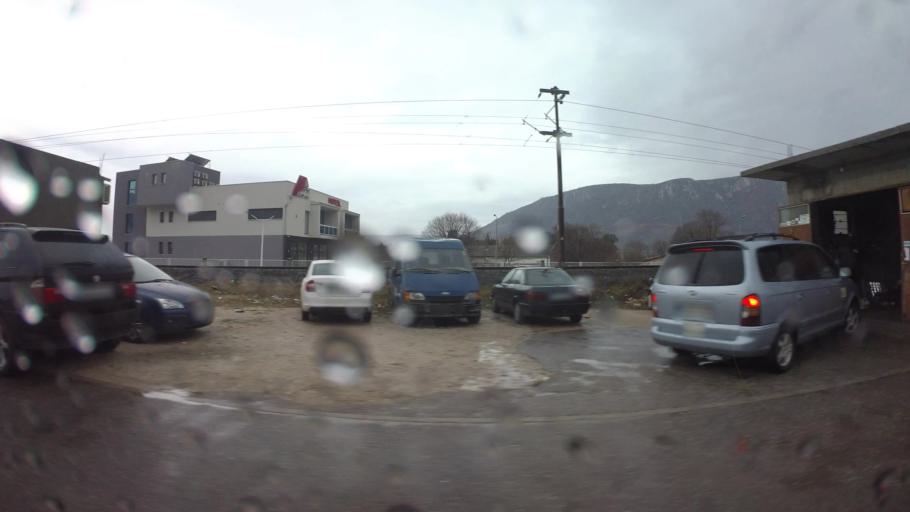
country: BA
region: Federation of Bosnia and Herzegovina
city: Rodoc
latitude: 43.3219
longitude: 17.8316
